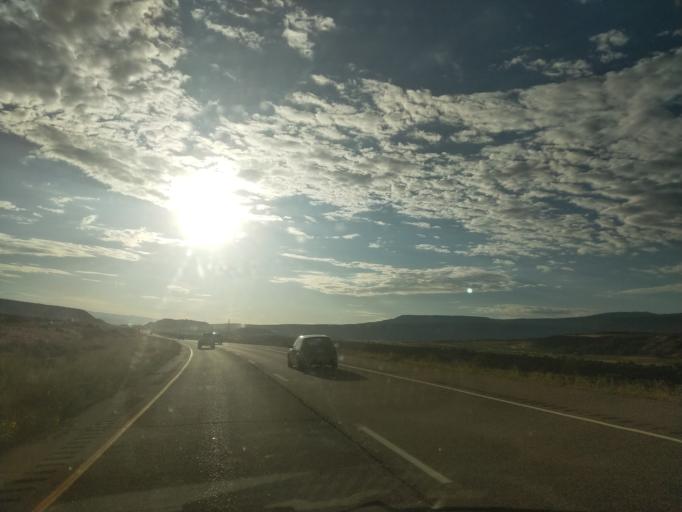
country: US
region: Colorado
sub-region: Garfield County
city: Battlement Mesa
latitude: 39.4987
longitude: -107.9183
